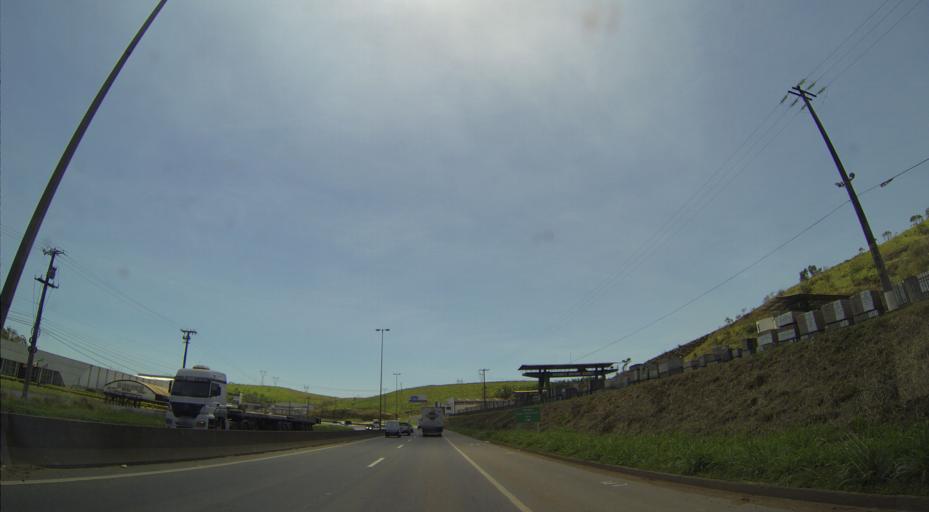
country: BR
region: Espirito Santo
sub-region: Viana
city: Viana
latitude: -20.3770
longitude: -40.4452
